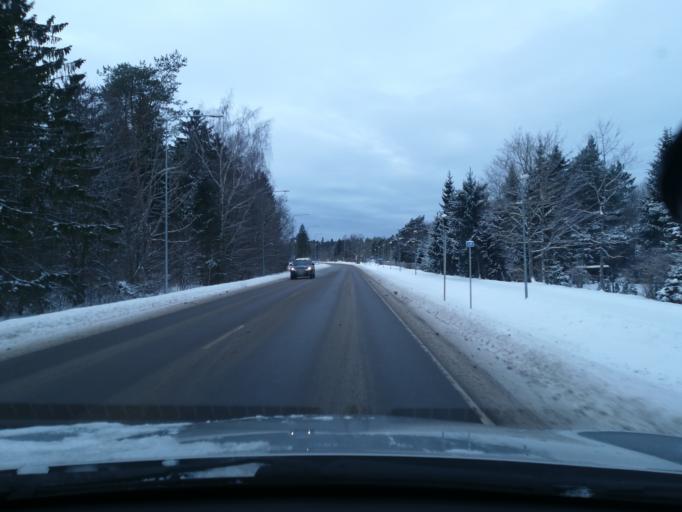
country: EE
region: Harju
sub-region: Harku vald
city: Tabasalu
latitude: 59.4353
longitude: 24.5199
